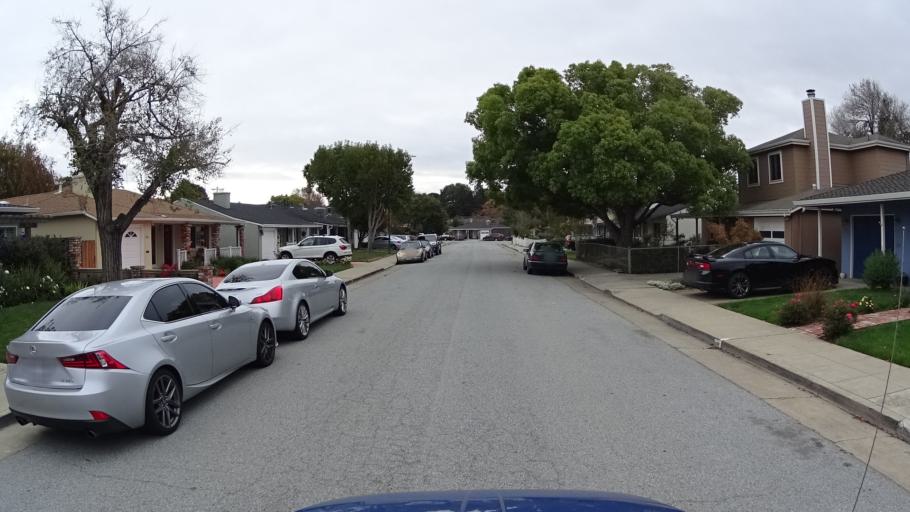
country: US
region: California
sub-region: San Mateo County
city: Belmont
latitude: 37.5351
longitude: -122.2867
